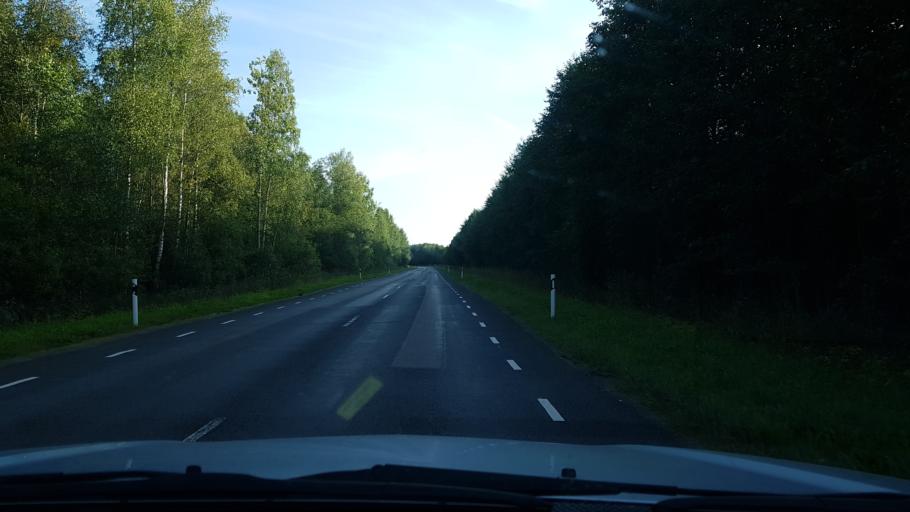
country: EE
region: Ida-Virumaa
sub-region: Sillamaee linn
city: Sillamae
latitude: 59.3146
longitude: 27.9128
